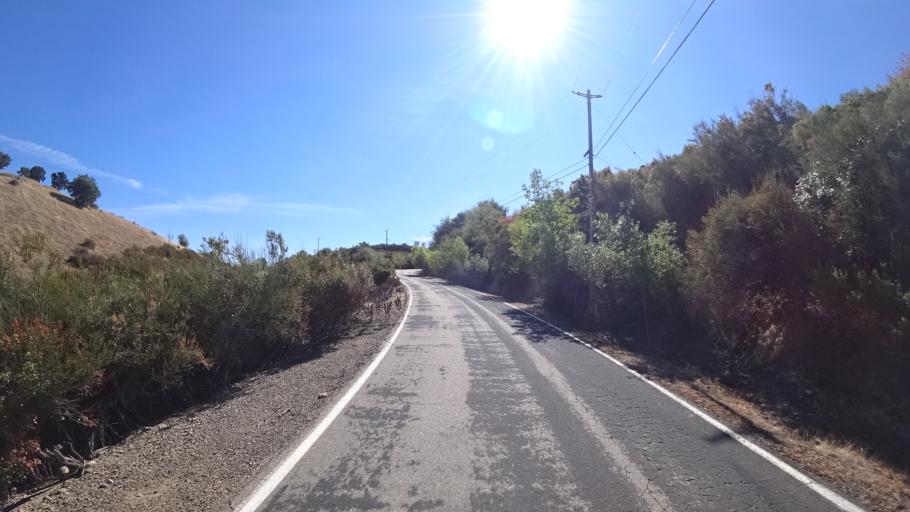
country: US
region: California
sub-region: Calaveras County
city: Valley Springs
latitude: 38.1731
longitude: -120.8649
